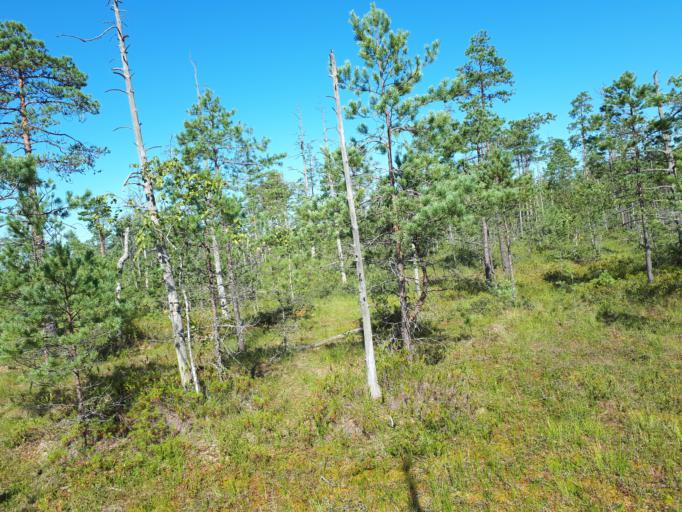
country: BY
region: Vitebsk
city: Rasony
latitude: 56.0591
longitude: 28.6291
